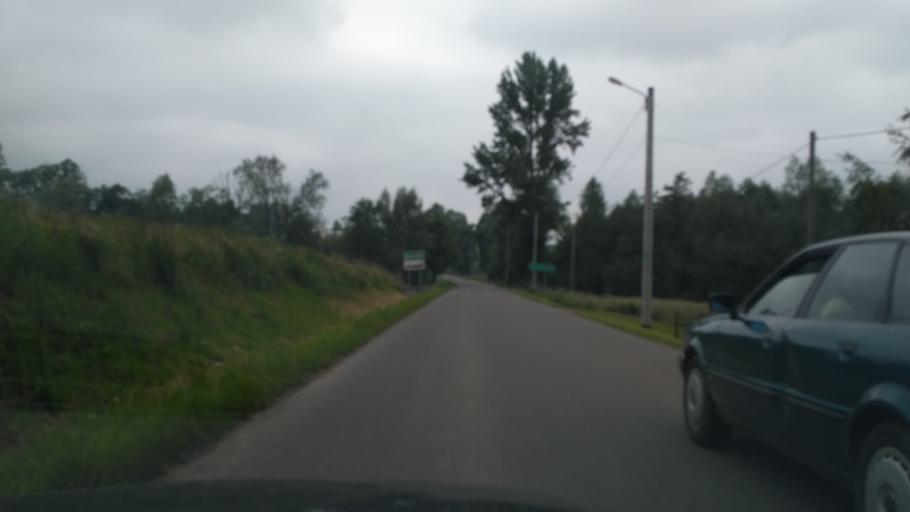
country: PL
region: Subcarpathian Voivodeship
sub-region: Powiat ropczycko-sedziszowski
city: Sedziszow Malopolski
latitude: 50.0452
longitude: 21.6993
